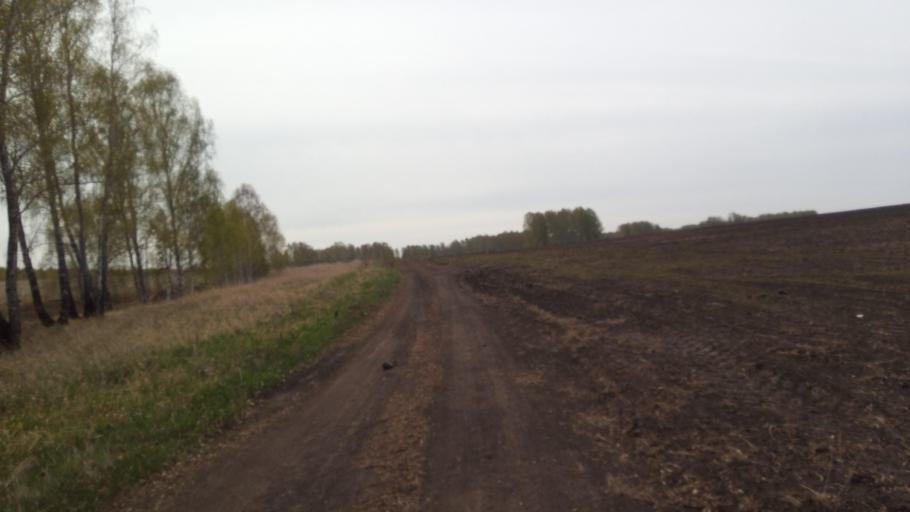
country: RU
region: Chelyabinsk
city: Timiryazevskiy
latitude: 55.0160
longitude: 60.8574
